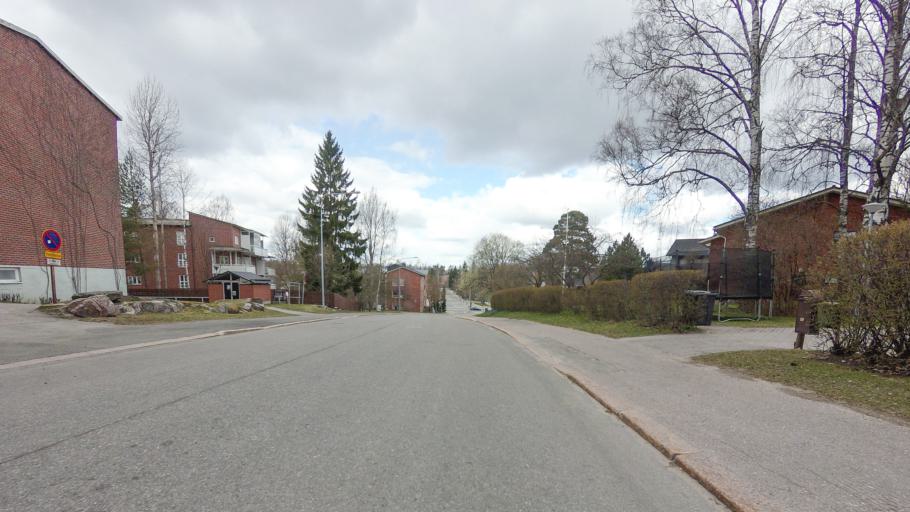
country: FI
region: Uusimaa
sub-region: Helsinki
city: Vantaa
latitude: 60.2169
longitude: 25.1048
